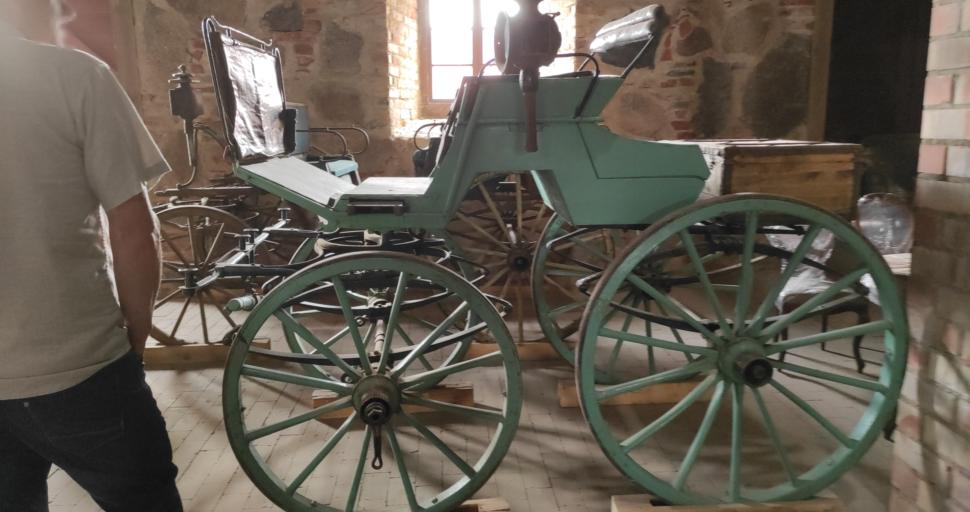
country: LV
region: Talsu Rajons
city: Talsi
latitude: 57.2267
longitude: 22.7627
